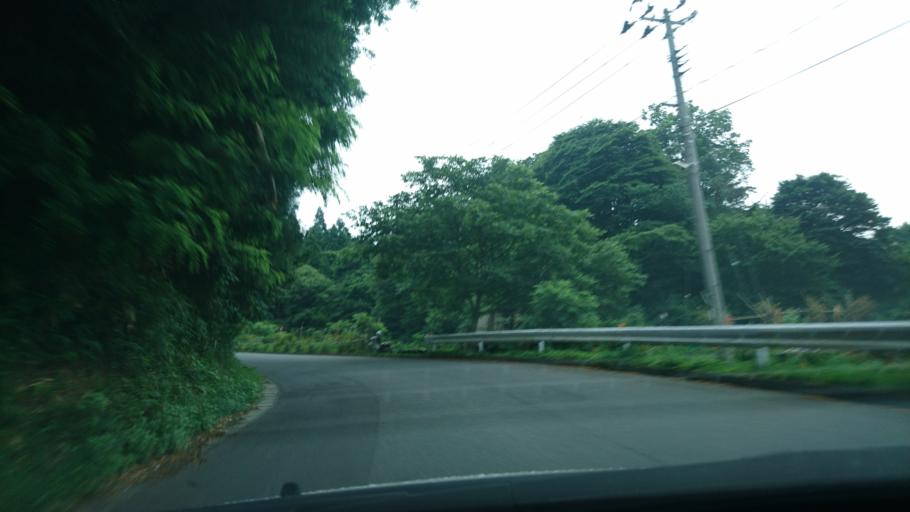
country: JP
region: Iwate
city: Ichinoseki
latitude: 38.9261
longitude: 141.1632
